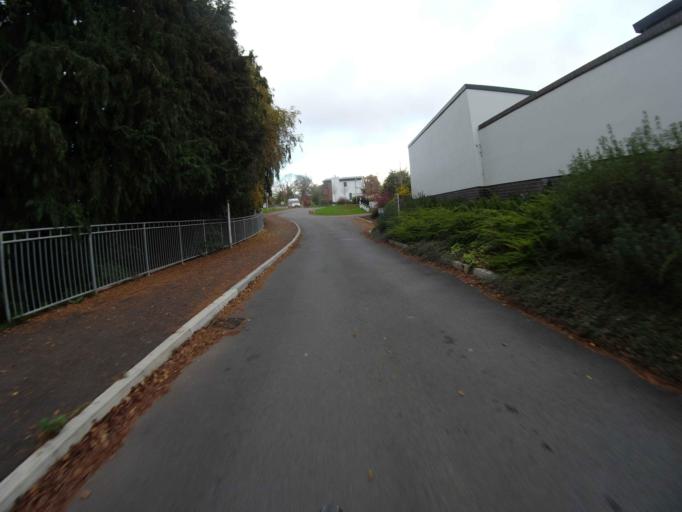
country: GB
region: England
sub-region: Devon
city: Topsham
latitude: 50.7022
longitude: -3.4808
